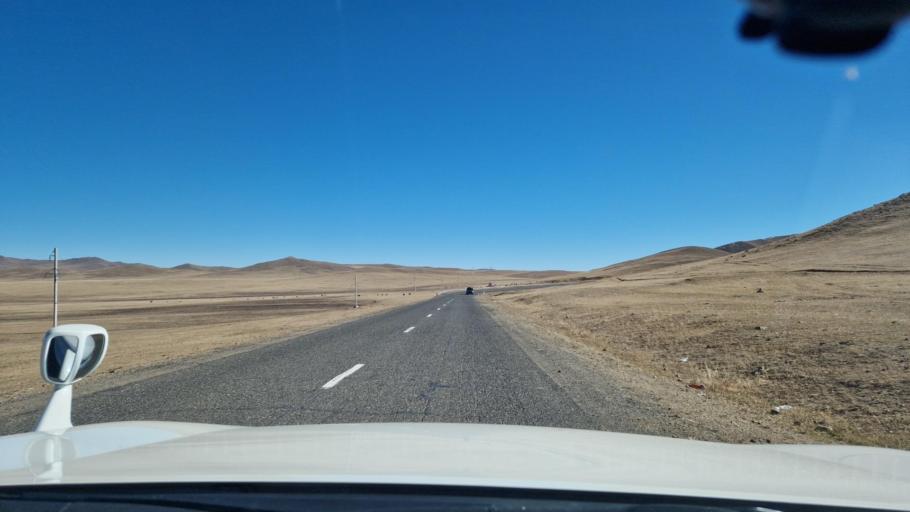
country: MN
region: Hentiy
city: Modot
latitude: 47.7604
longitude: 108.9284
